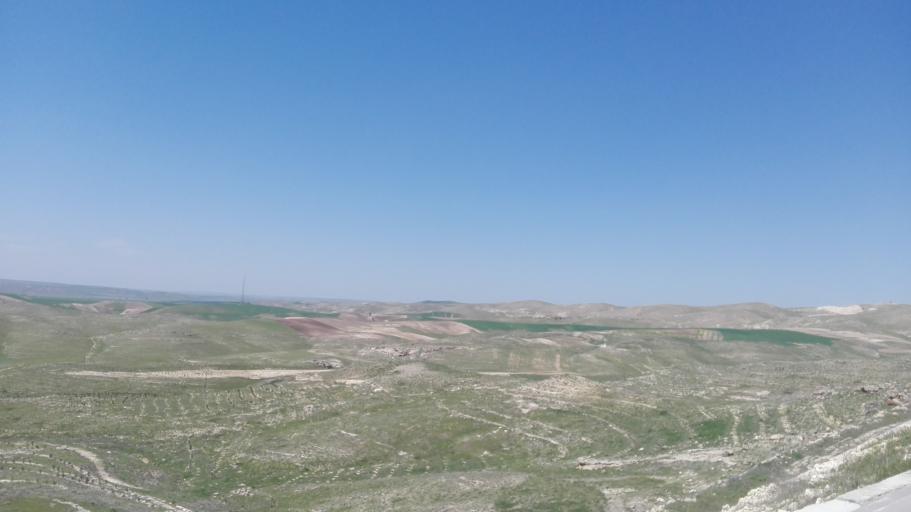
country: TR
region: Batman
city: Oymatas
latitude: 37.7850
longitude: 41.0618
